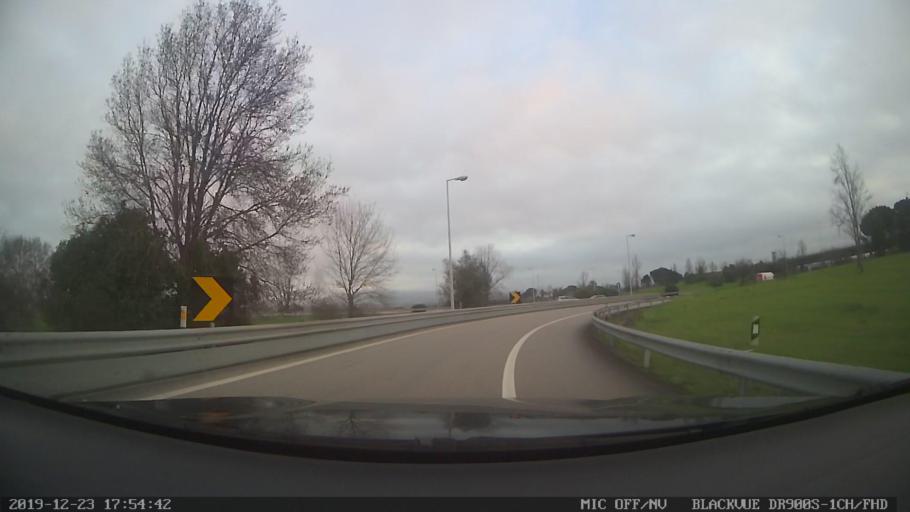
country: PT
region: Aveiro
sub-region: Mealhada
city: Mealhada
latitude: 40.3756
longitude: -8.4944
